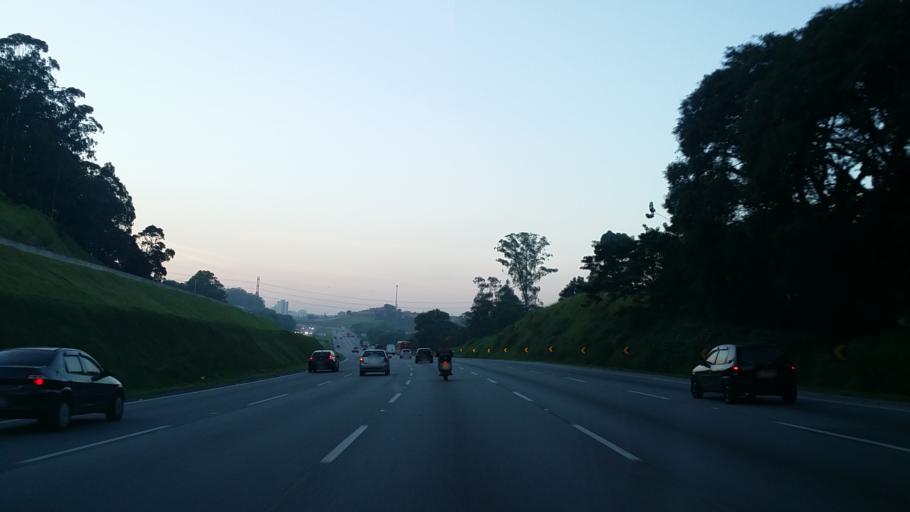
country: BR
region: Sao Paulo
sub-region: Osasco
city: Osasco
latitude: -23.4628
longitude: -46.7523
